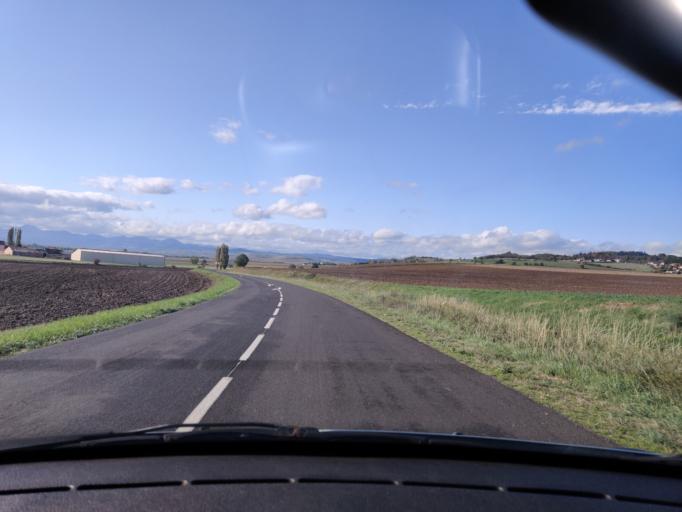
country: FR
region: Auvergne
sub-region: Departement du Puy-de-Dome
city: Aigueperse
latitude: 46.0105
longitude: 3.1841
